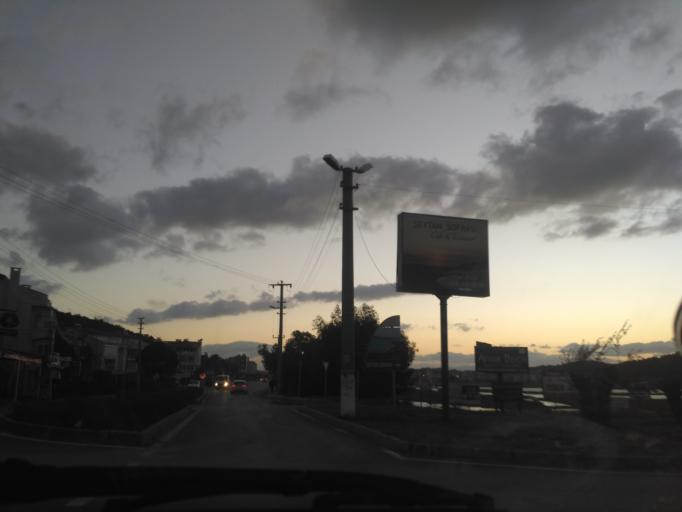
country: TR
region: Balikesir
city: Ayvalik
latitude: 39.2787
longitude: 26.6709
